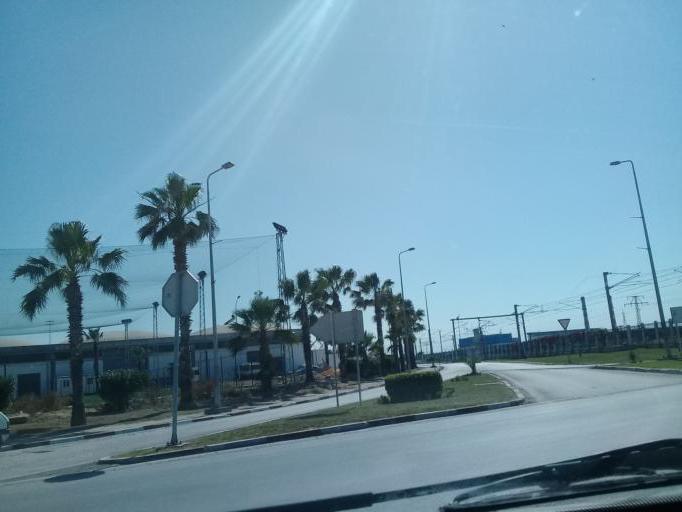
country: TN
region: Tunis
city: La Goulette
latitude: 36.8163
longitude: 10.2985
